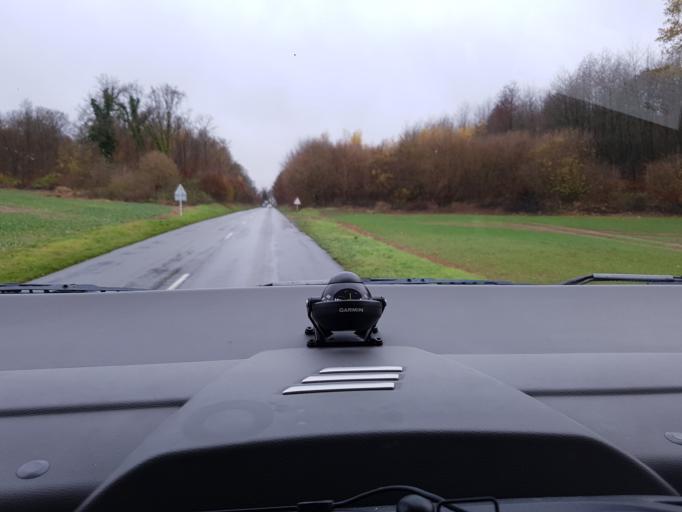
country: FR
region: Haute-Normandie
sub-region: Departement de l'Eure
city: Pont-Saint-Pierre
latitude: 49.3292
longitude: 1.2951
